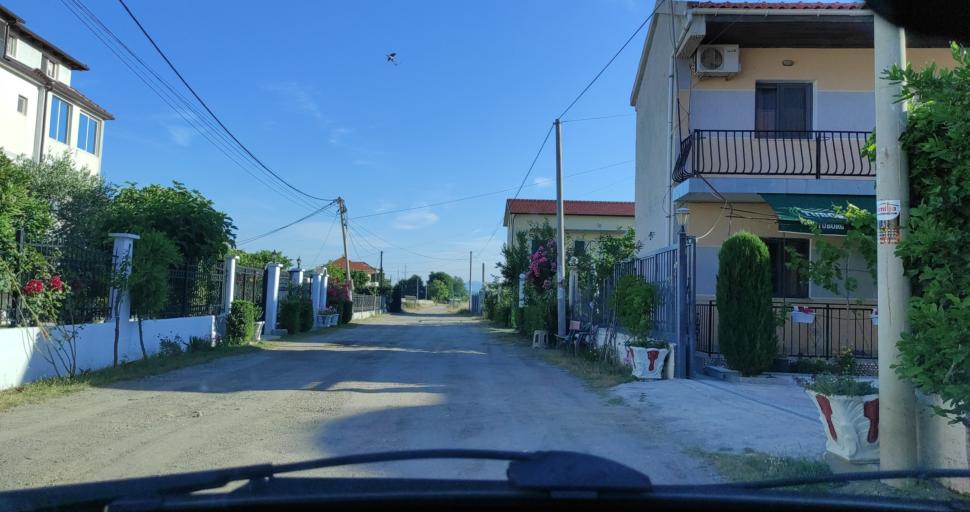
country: AL
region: Shkoder
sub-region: Rrethi i Shkodres
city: Velipoje
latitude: 41.8665
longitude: 19.4286
